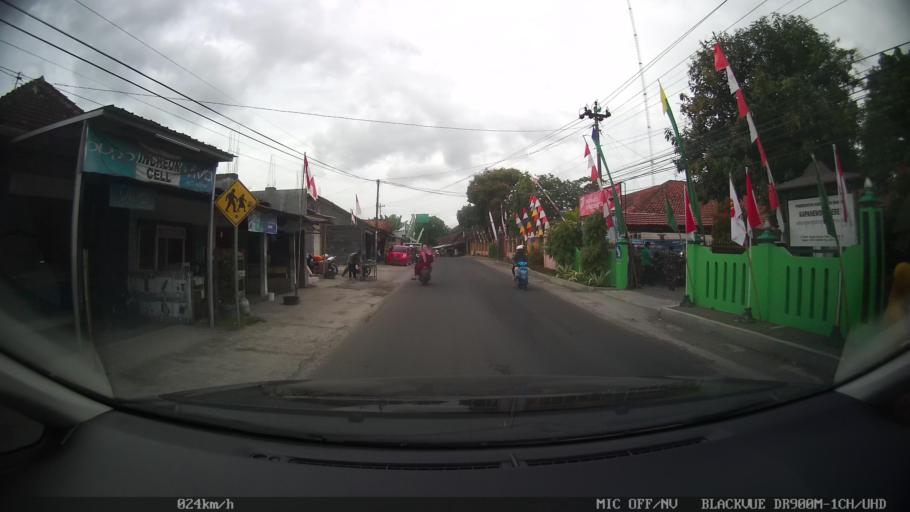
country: ID
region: Daerah Istimewa Yogyakarta
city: Sewon
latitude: -7.8663
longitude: 110.4078
